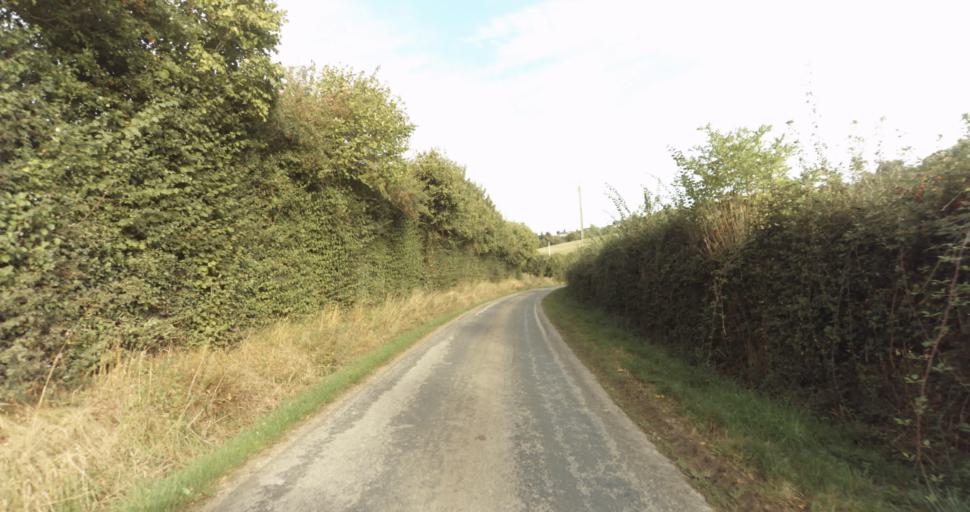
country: FR
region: Lower Normandy
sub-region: Departement de l'Orne
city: Vimoutiers
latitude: 48.8727
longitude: 0.2395
